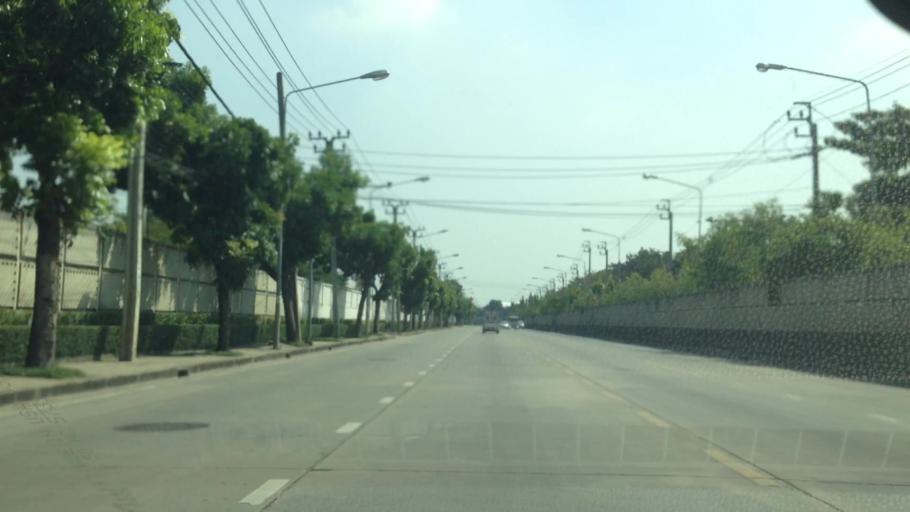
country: TH
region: Bangkok
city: Sai Mai
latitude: 13.9218
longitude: 100.6281
